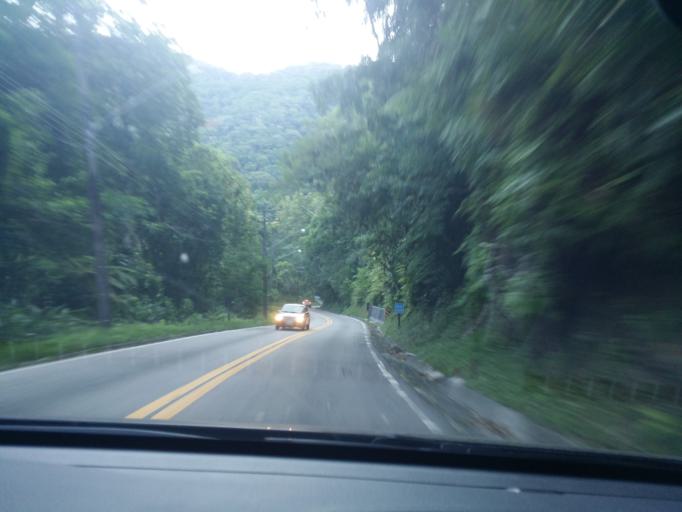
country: BR
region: Sao Paulo
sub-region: Sao Sebastiao
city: Sao Sebastiao
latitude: -23.7828
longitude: -45.5968
